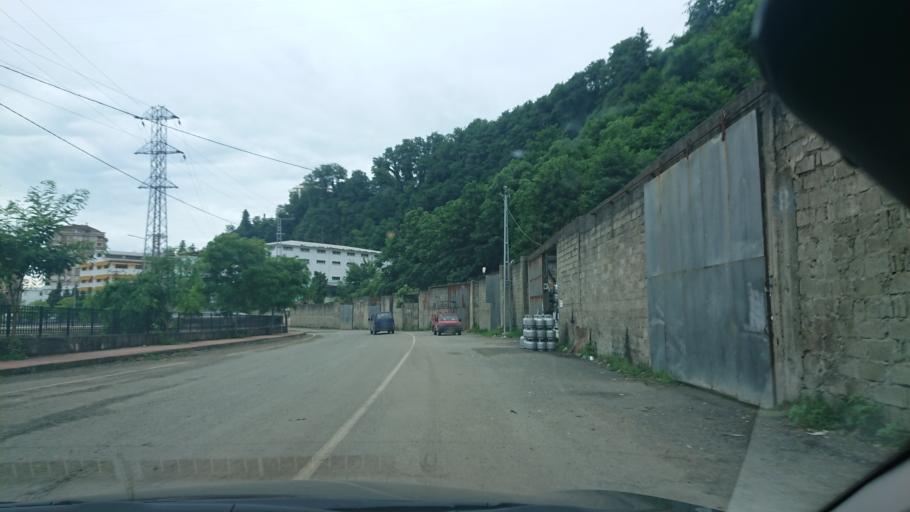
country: TR
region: Rize
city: Rize
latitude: 41.0310
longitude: 40.4829
